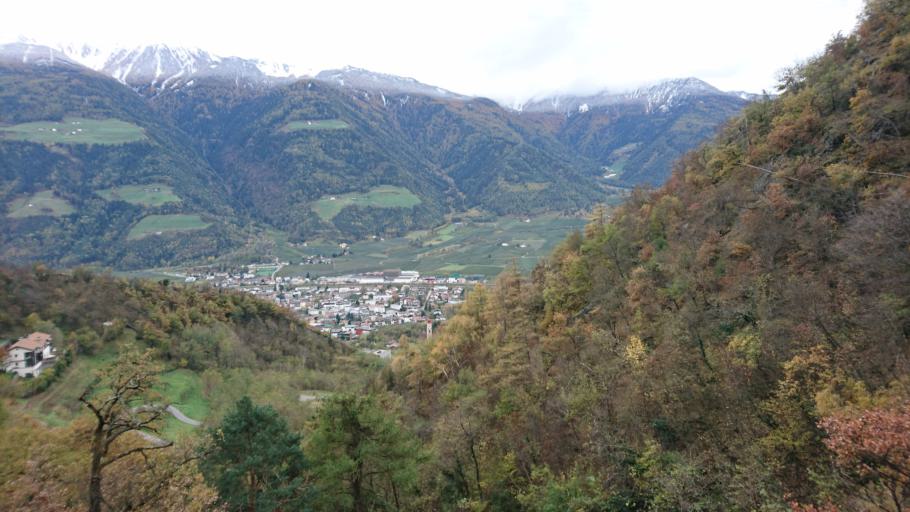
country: IT
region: Trentino-Alto Adige
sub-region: Bolzano
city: Naturno
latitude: 46.6587
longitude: 11.0015
